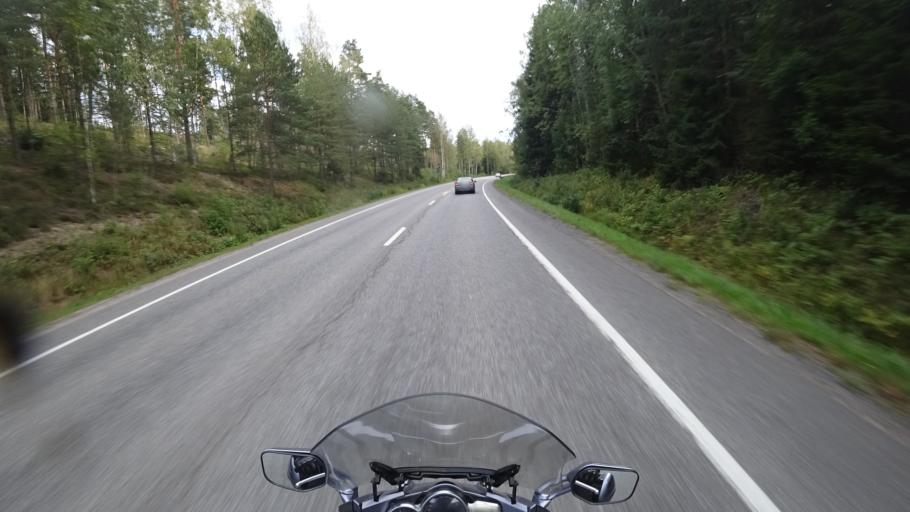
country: FI
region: Uusimaa
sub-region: Raaseporin
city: Karis
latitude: 60.0846
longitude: 23.6594
